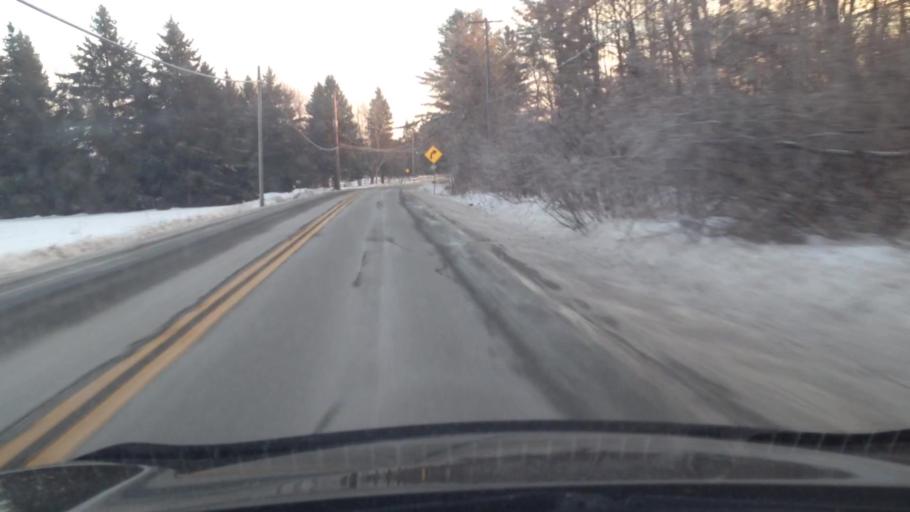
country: CA
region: Quebec
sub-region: Lanaudiere
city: Sainte-Julienne
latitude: 45.9181
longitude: -73.7387
